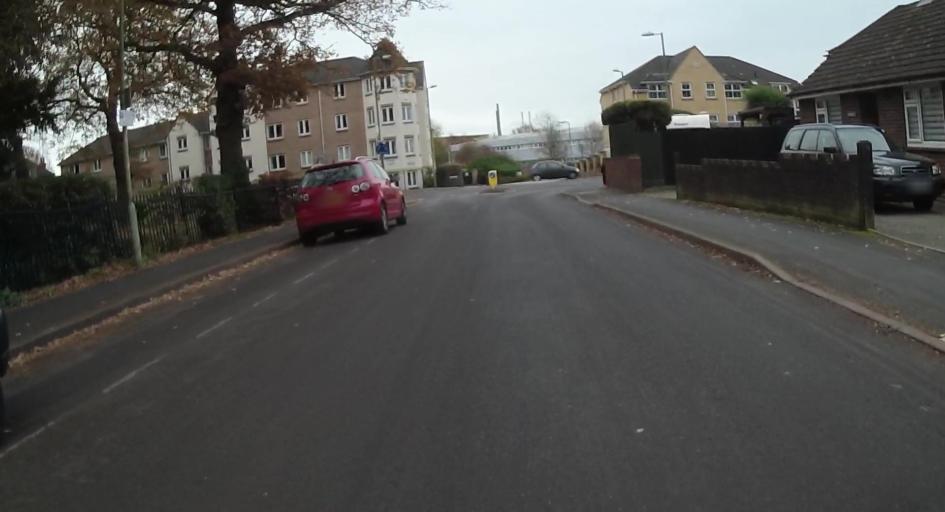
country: GB
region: England
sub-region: Hampshire
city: Farnborough
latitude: 51.2938
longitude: -0.7598
